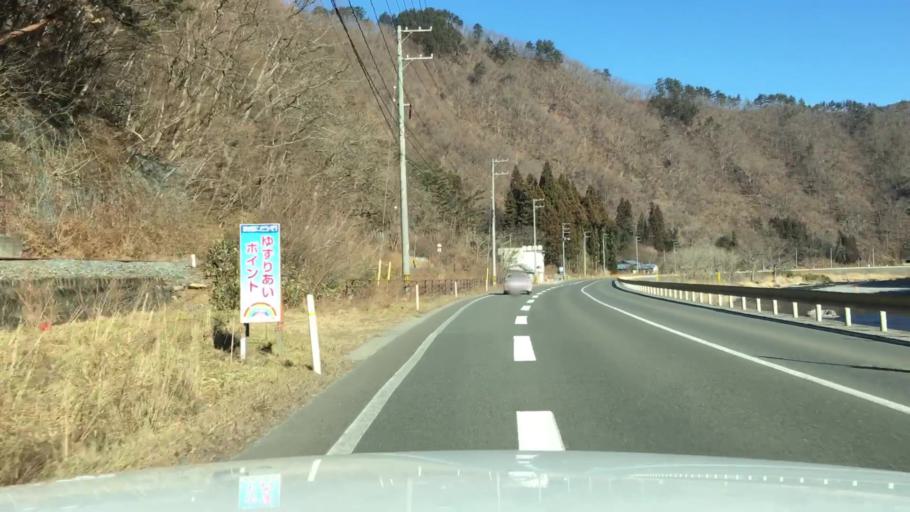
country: JP
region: Iwate
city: Miyako
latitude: 39.6133
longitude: 141.7882
